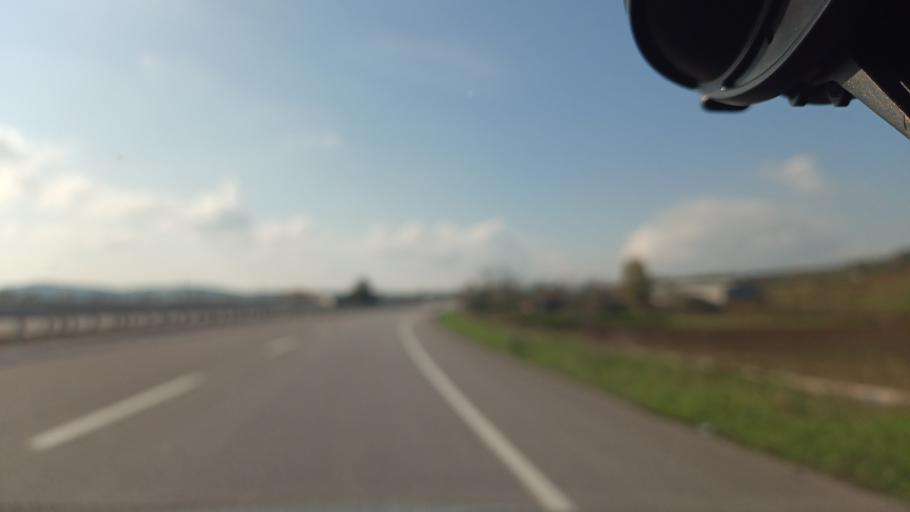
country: TR
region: Sakarya
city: Kaynarca
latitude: 41.0367
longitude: 30.3341
